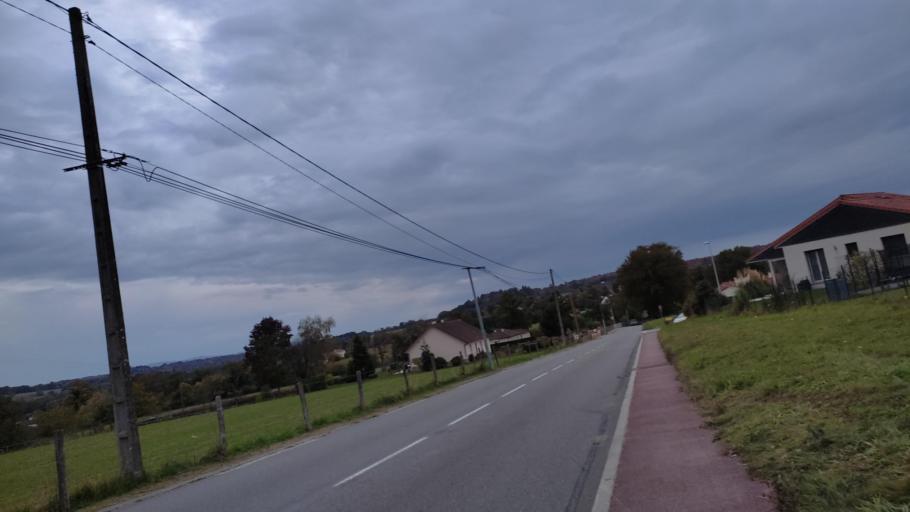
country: FR
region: Limousin
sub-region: Departement de la Haute-Vienne
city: Isle
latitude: 45.8317
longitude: 1.2078
